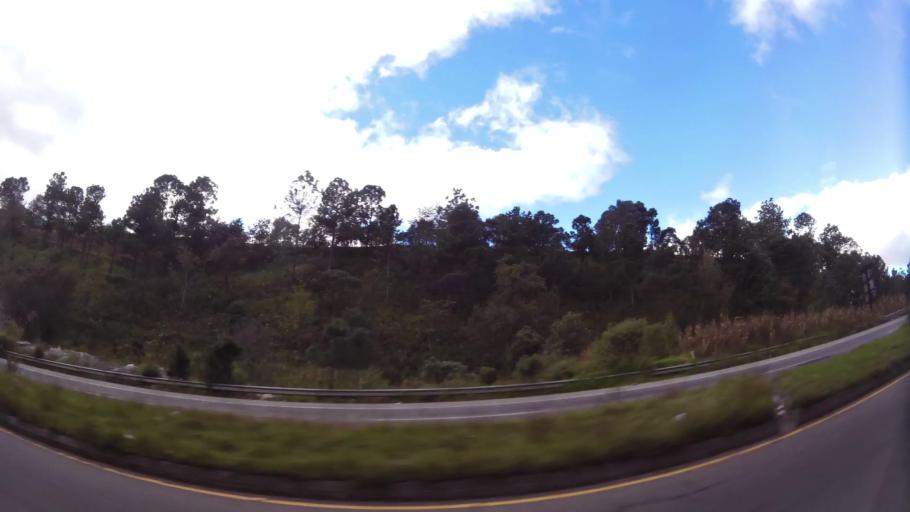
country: GT
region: Quetzaltenango
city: Salcaja
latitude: 14.8720
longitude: -91.4714
